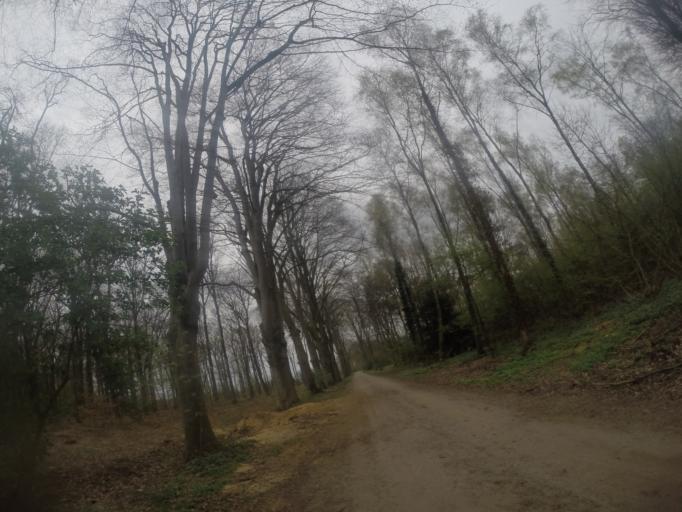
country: NL
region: Gelderland
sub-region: Gemeente Zutphen
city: Leesten
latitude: 52.1231
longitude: 6.2683
